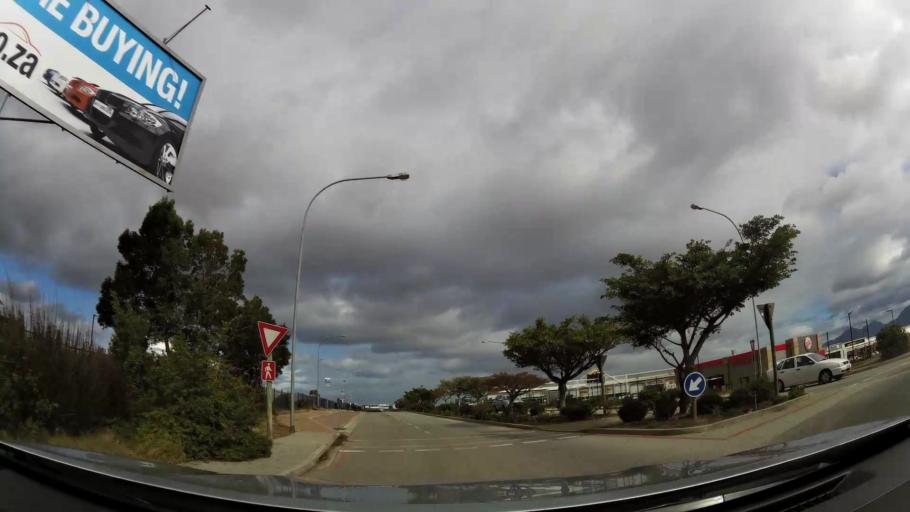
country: ZA
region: Western Cape
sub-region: Eden District Municipality
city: George
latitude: -33.9854
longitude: 22.5016
